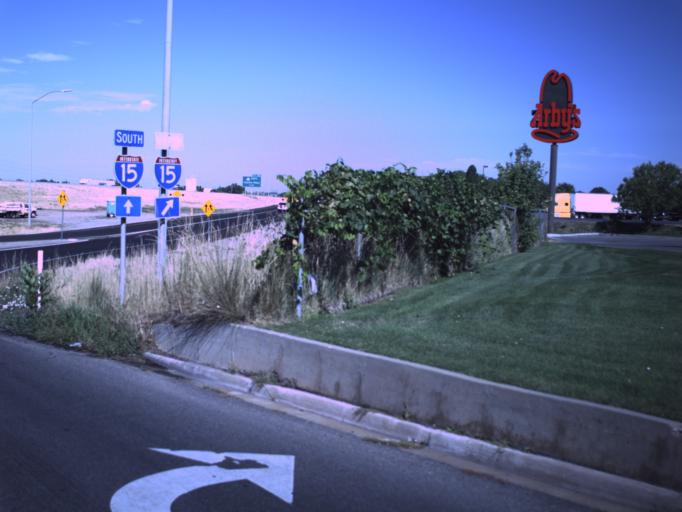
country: US
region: Utah
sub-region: Davis County
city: Kaysville
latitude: 41.0382
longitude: -111.9467
